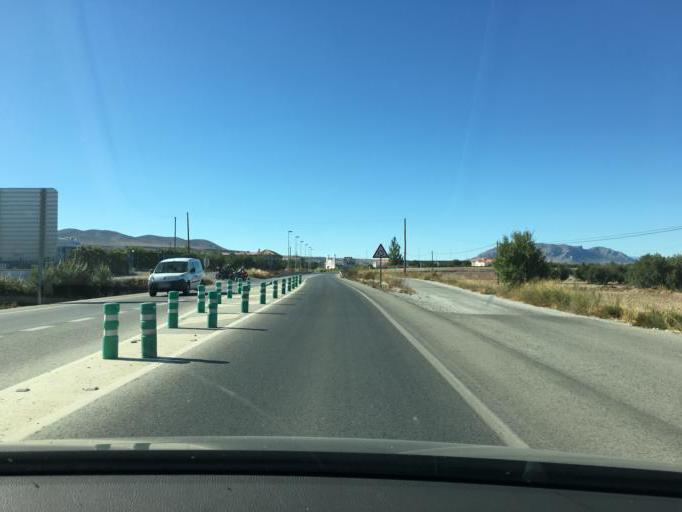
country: ES
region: Andalusia
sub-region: Provincia de Granada
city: Caniles
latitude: 37.4522
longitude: -2.7347
